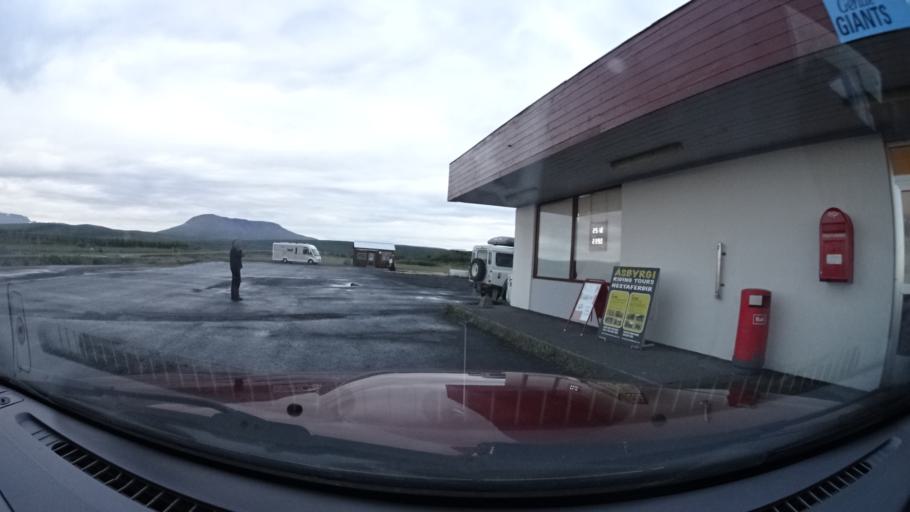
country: IS
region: Northeast
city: Husavik
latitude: 66.0305
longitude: -16.4836
